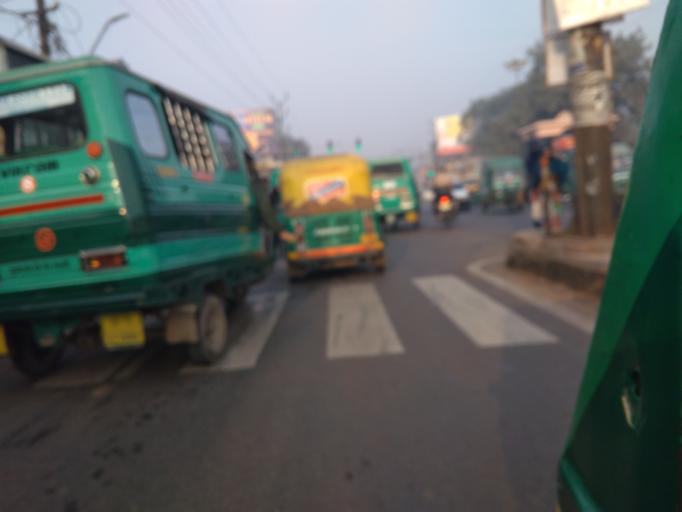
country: IN
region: Uttar Pradesh
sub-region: Kanpur
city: Nawabganj
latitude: 26.4831
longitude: 80.2991
